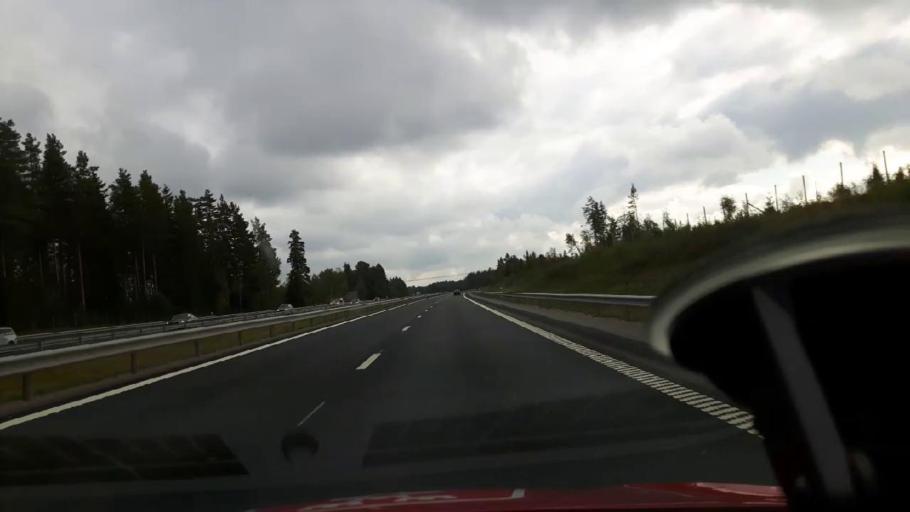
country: SE
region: Gaevleborg
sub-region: Gavle Kommun
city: Gavle
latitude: 60.6302
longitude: 17.1508
